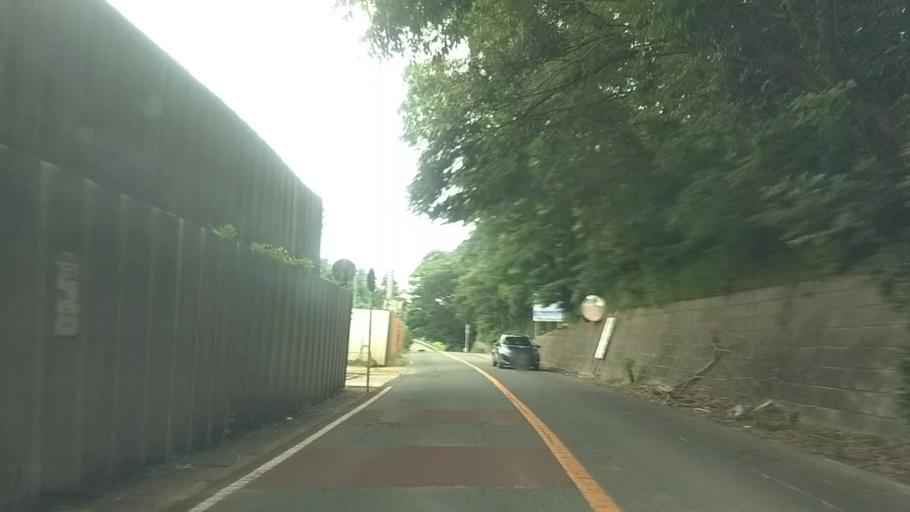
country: JP
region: Kanagawa
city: Fujisawa
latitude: 35.3582
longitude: 139.4355
